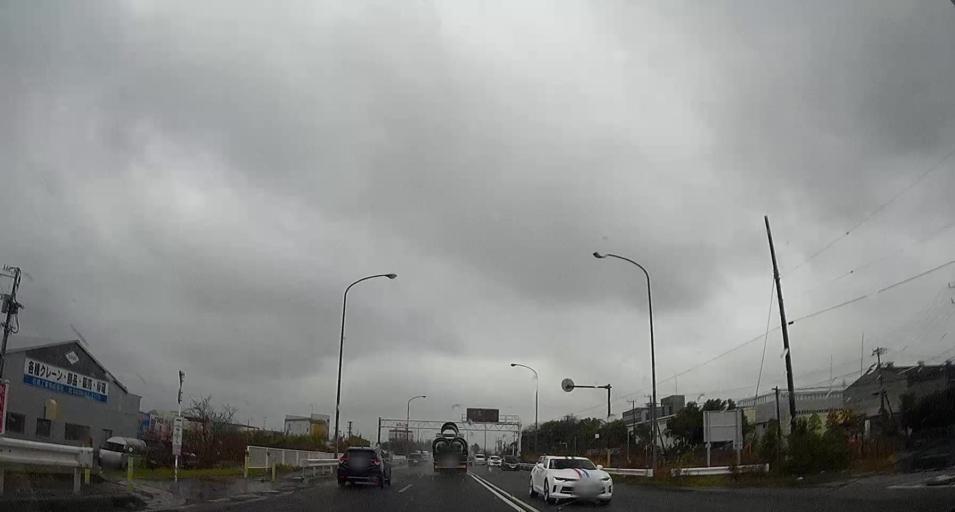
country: JP
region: Chiba
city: Ichihara
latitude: 35.5441
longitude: 140.1189
